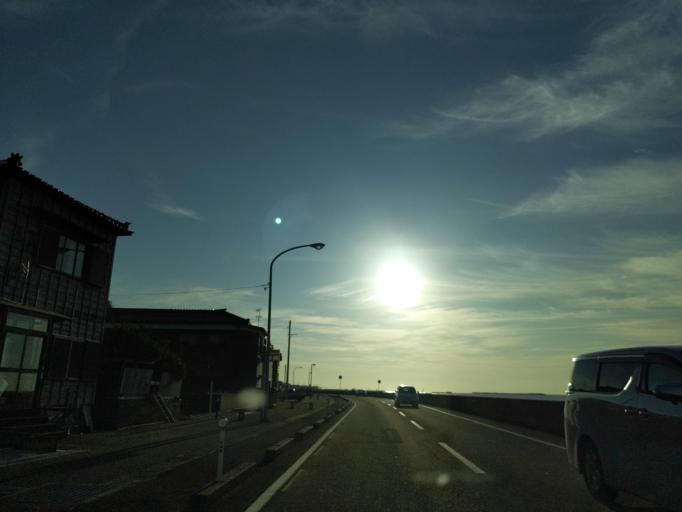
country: JP
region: Niigata
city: Nagaoka
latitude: 37.5512
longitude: 138.7003
